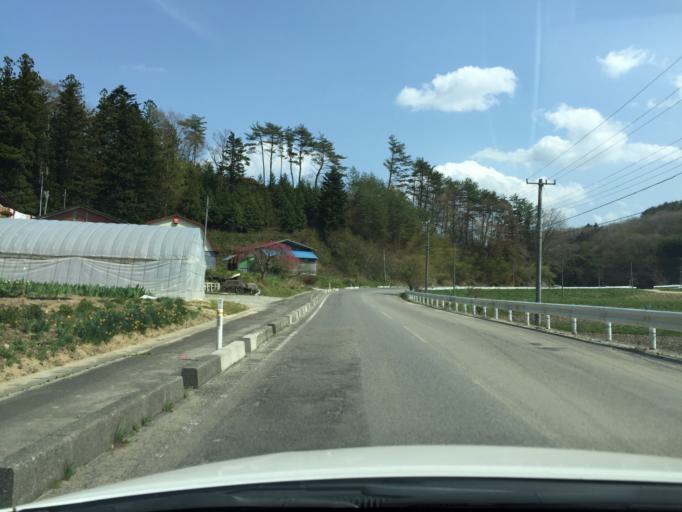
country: JP
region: Fukushima
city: Namie
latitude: 37.4013
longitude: 140.8008
